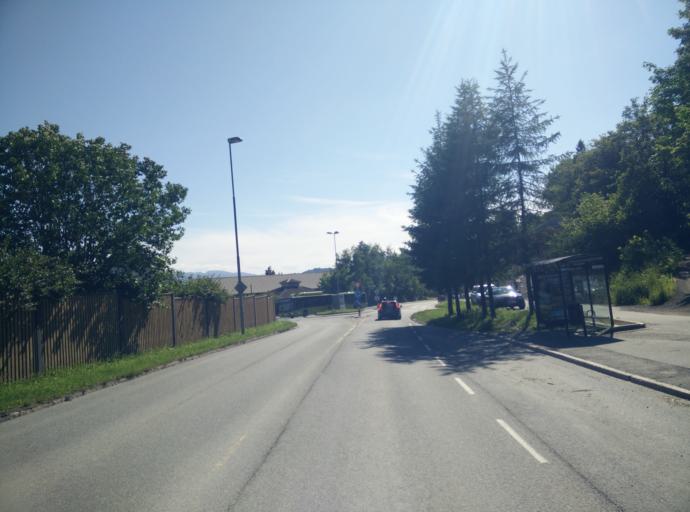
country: NO
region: Sor-Trondelag
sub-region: Trondheim
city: Trondheim
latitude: 63.3987
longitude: 10.3579
